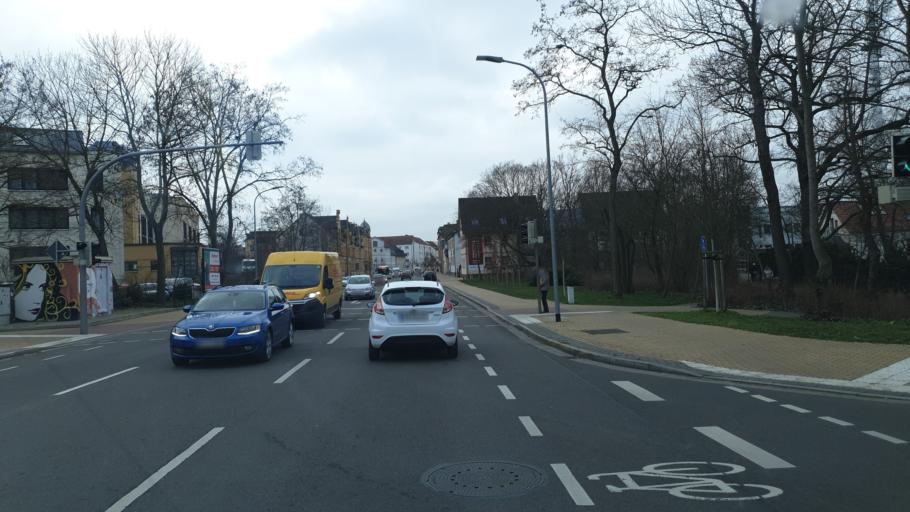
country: DE
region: Saxony
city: Delitzsch
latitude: 51.5282
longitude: 12.3363
